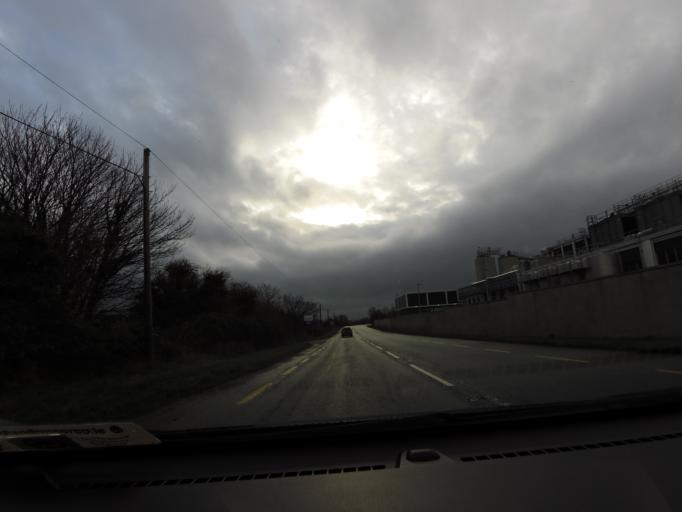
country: IE
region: Leinster
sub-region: Kilkenny
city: Ballyragget
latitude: 52.8012
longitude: -7.3508
